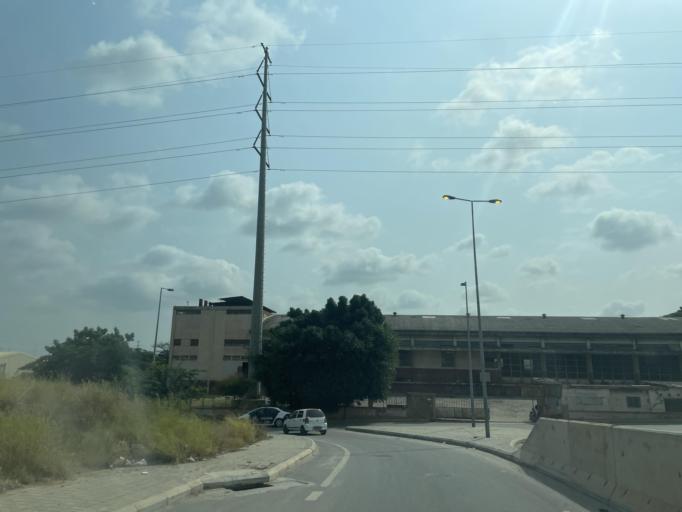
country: AO
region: Luanda
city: Luanda
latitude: -8.8053
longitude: 13.2527
